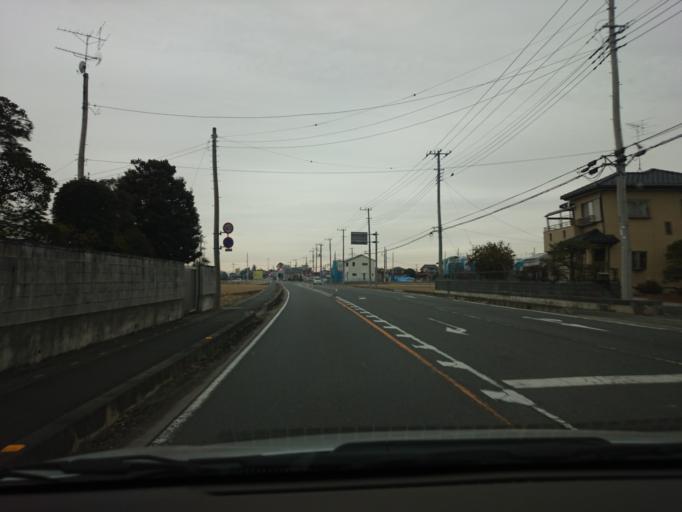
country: JP
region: Saitama
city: Kisai
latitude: 36.1093
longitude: 139.5893
